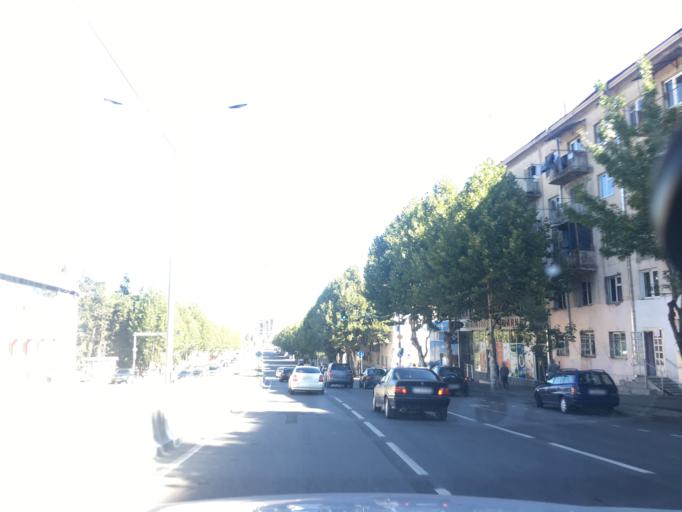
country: GE
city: Zahesi
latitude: 41.7739
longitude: 44.7946
